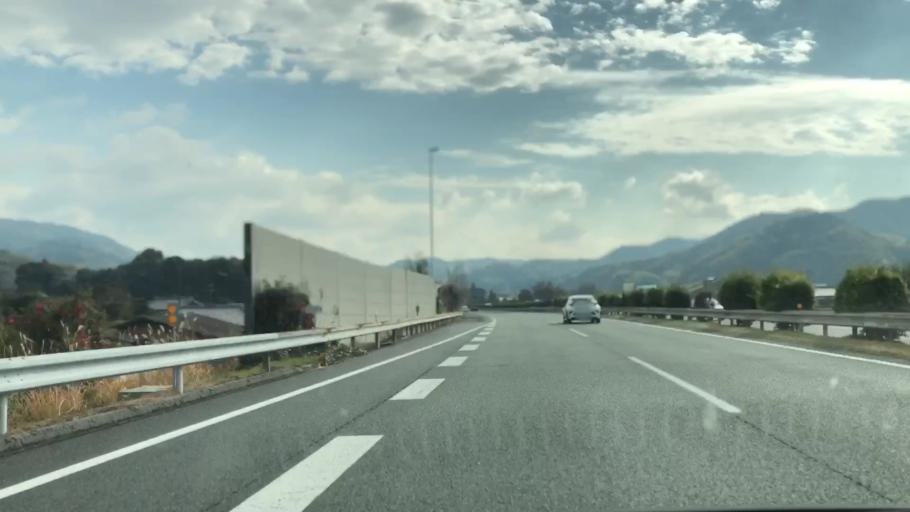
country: JP
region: Fukuoka
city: Setakamachi-takayanagi
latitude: 33.1256
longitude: 130.5184
